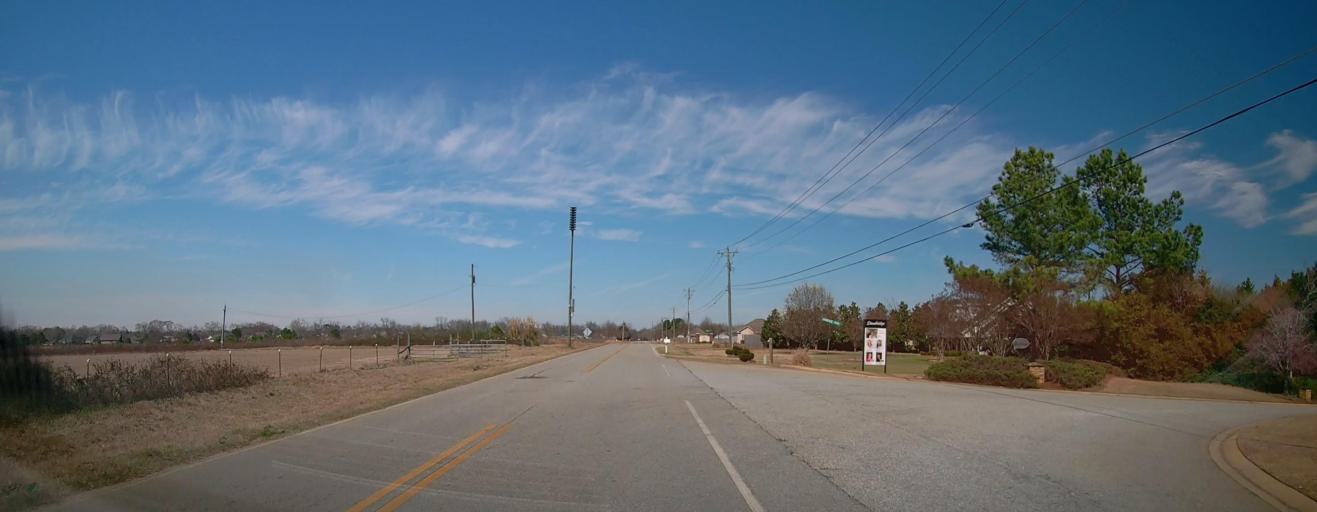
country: US
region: Georgia
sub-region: Houston County
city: Perry
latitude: 32.4550
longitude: -83.6827
